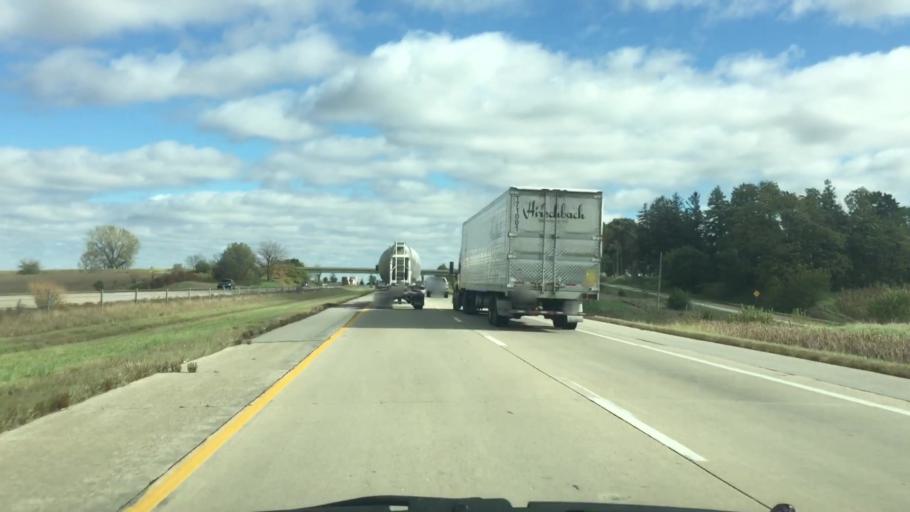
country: US
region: Iowa
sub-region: Poweshiek County
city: Brooklyn
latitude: 41.6960
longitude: -92.4007
